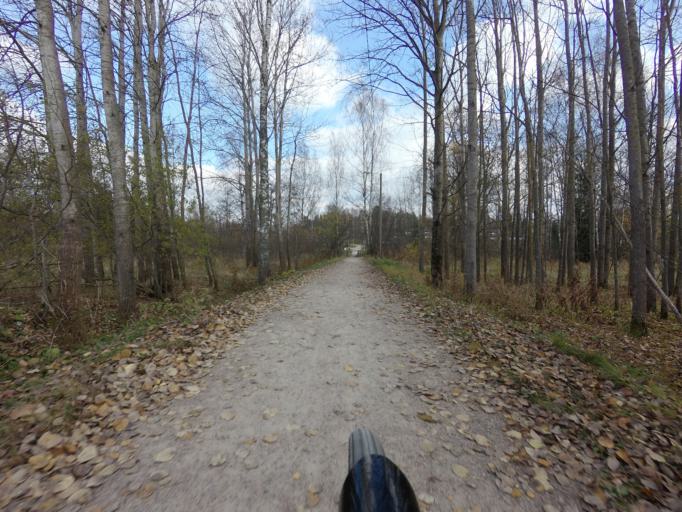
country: FI
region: Uusimaa
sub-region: Helsinki
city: Kauniainen
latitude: 60.1721
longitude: 24.7007
